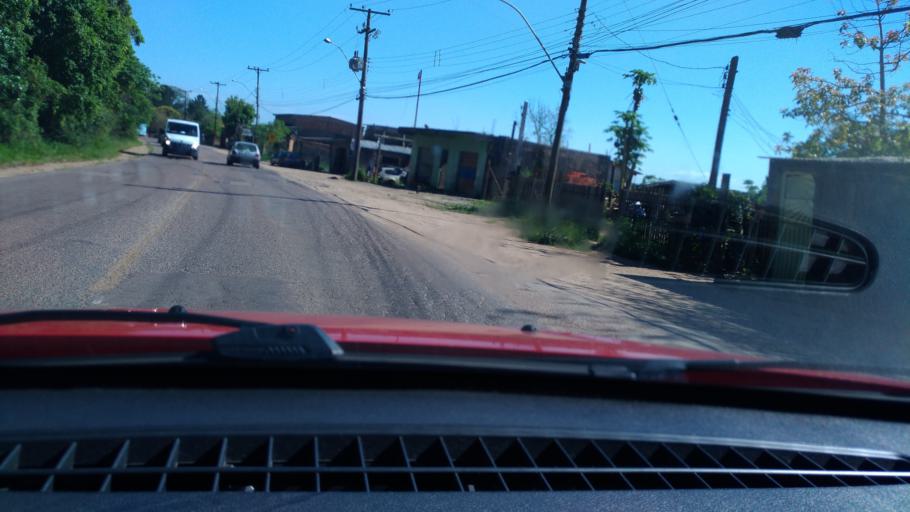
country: BR
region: Rio Grande do Sul
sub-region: Viamao
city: Viamao
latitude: -30.0528
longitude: -51.0606
